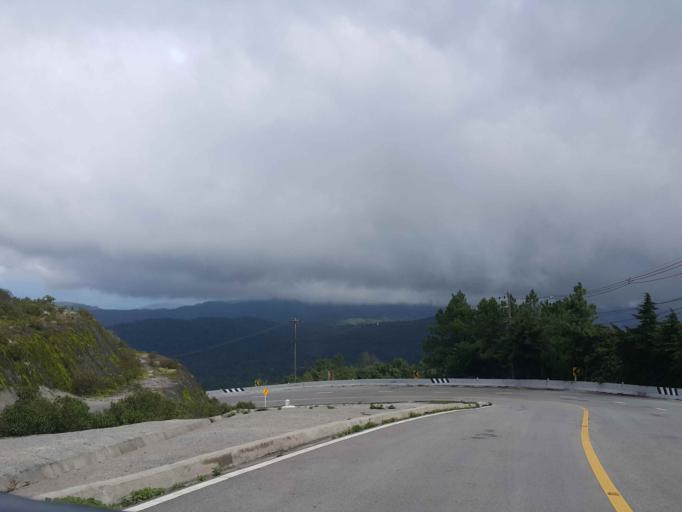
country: TH
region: Chiang Mai
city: Mae Chaem
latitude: 18.5487
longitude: 98.4829
